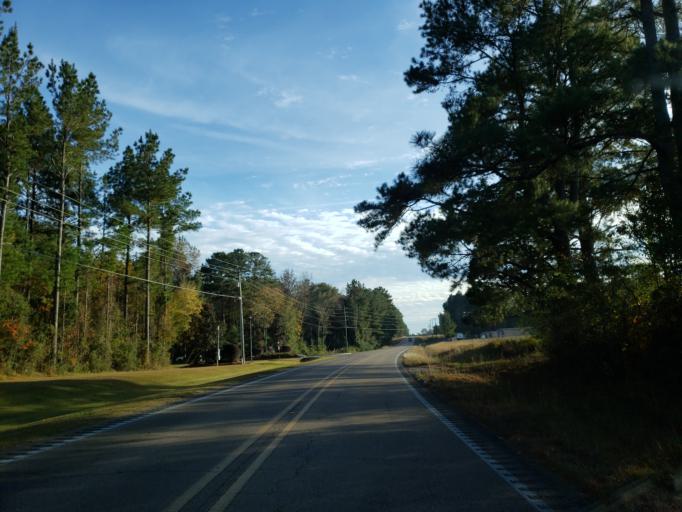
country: US
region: Mississippi
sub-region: Lamar County
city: West Hattiesburg
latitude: 31.2773
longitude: -89.4655
